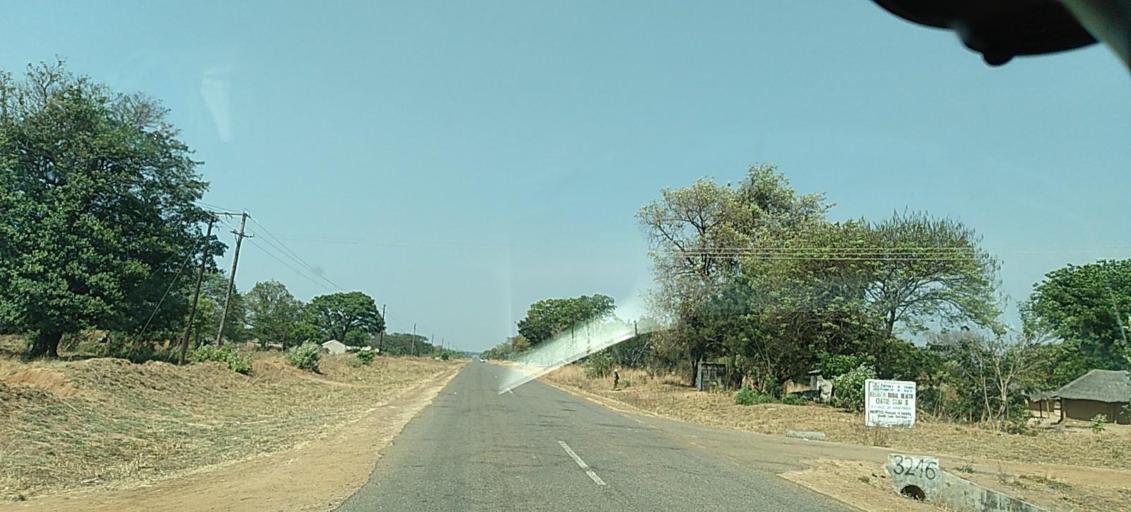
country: ZM
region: North-Western
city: Kabompo
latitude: -13.2598
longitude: 24.4959
